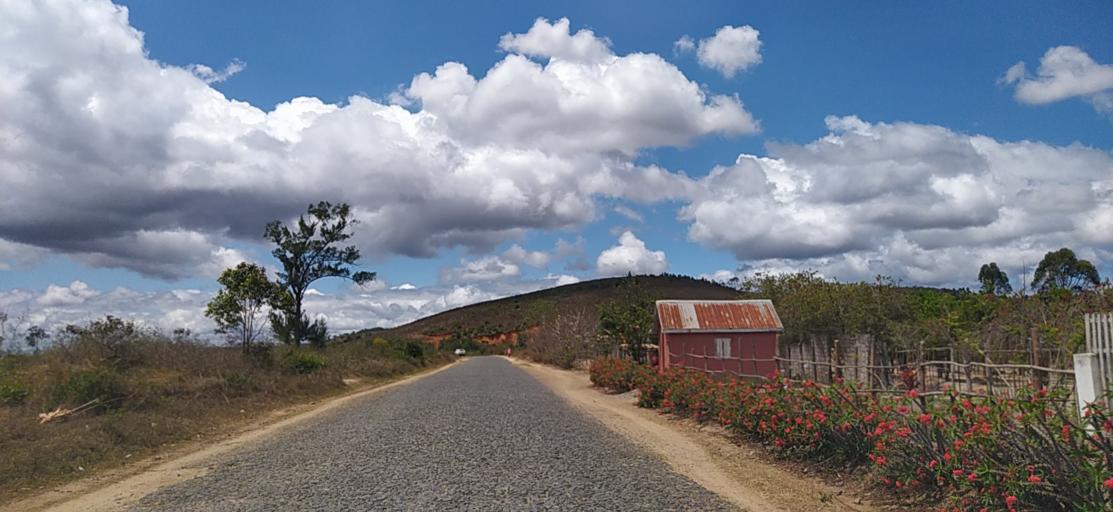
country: MG
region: Alaotra Mangoro
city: Moramanga
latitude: -18.7599
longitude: 48.2574
